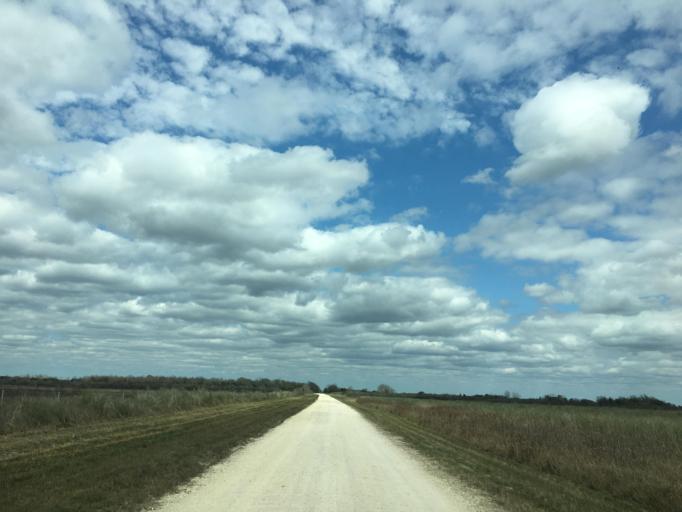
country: US
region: Texas
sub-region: Brazoria County
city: Oyster Creek
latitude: 29.0508
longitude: -95.2684
